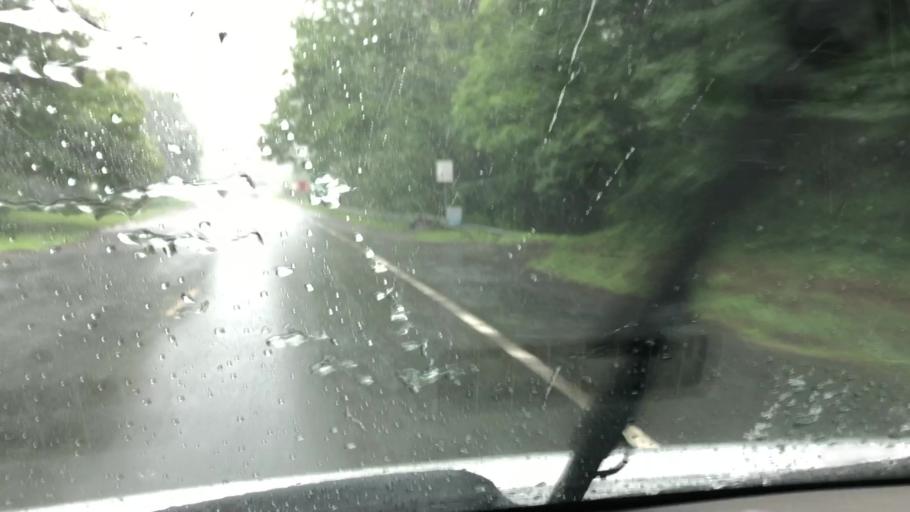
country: US
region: Massachusetts
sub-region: Hampshire County
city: Chesterfield
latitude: 42.4467
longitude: -72.8065
